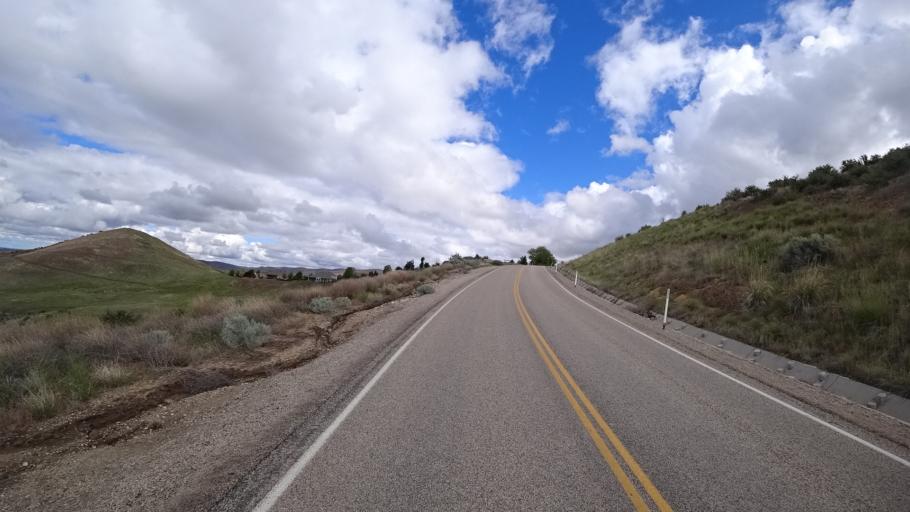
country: US
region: Idaho
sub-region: Ada County
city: Garden City
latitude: 43.7227
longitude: -116.2349
